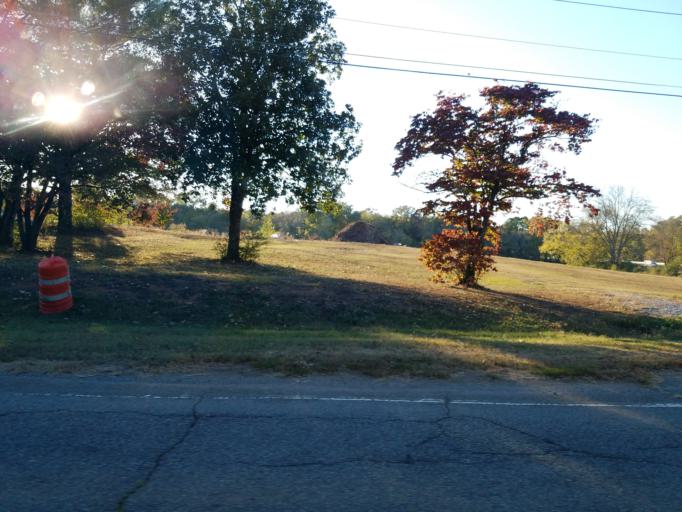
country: US
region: Georgia
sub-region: Bartow County
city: Adairsville
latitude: 34.3752
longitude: -84.9403
